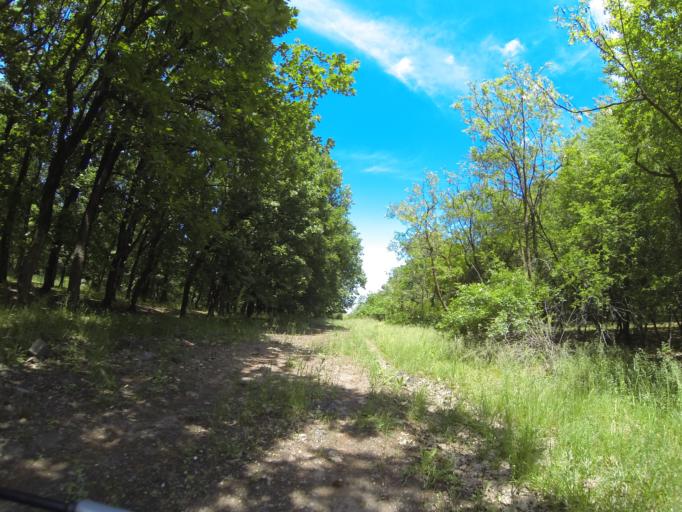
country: RO
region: Dolj
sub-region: Comuna Teslui
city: Teslui
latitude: 44.1695
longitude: 24.1656
